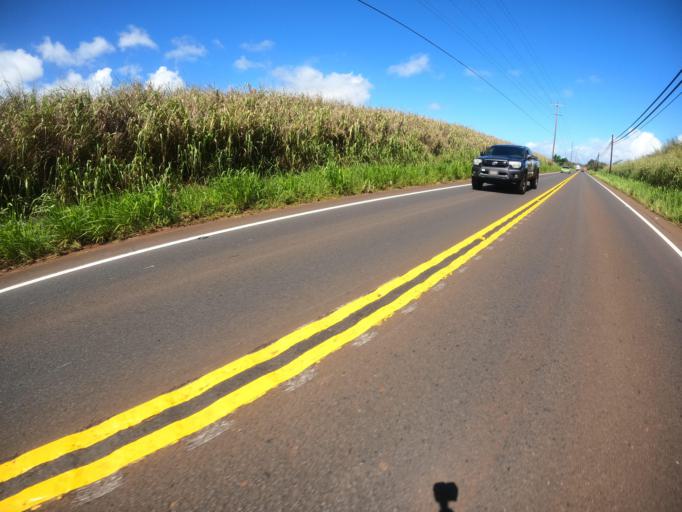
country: US
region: Hawaii
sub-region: Honolulu County
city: Schofield Barracks
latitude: 21.4645
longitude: -158.0554
